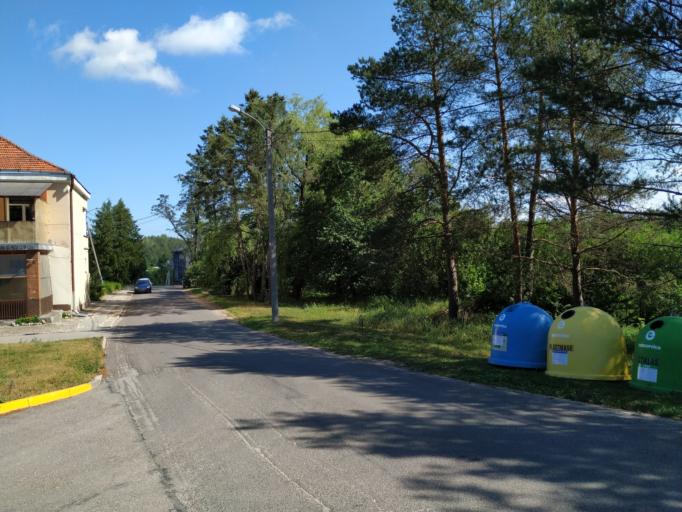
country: LT
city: Nemencine
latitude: 54.7944
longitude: 25.3975
